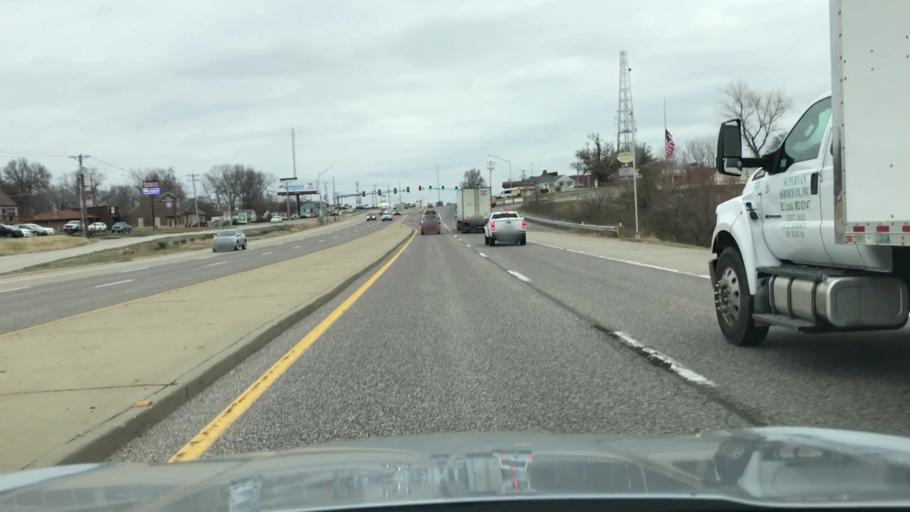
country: US
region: Missouri
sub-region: Saint Charles County
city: Saint Charles
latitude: 38.7731
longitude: -90.5186
